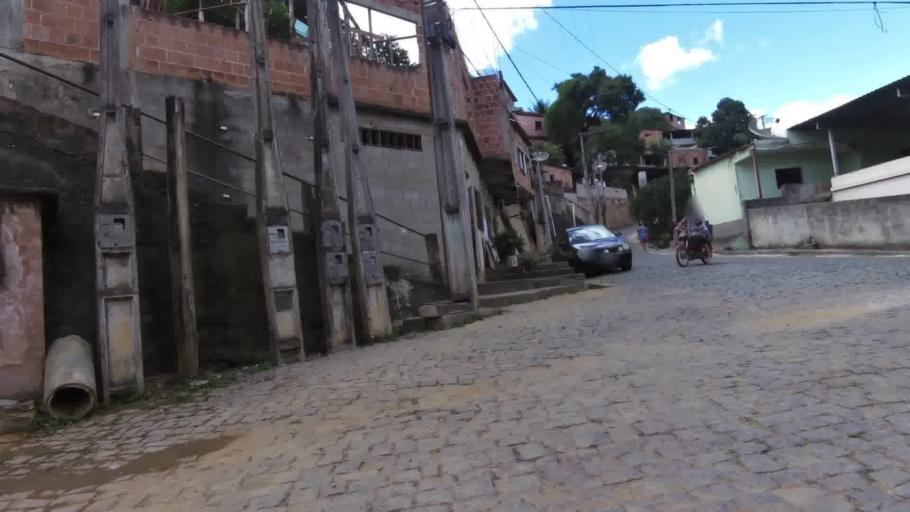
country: BR
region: Espirito Santo
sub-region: Rio Novo Do Sul
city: Rio Novo do Sul
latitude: -20.8665
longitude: -40.9434
